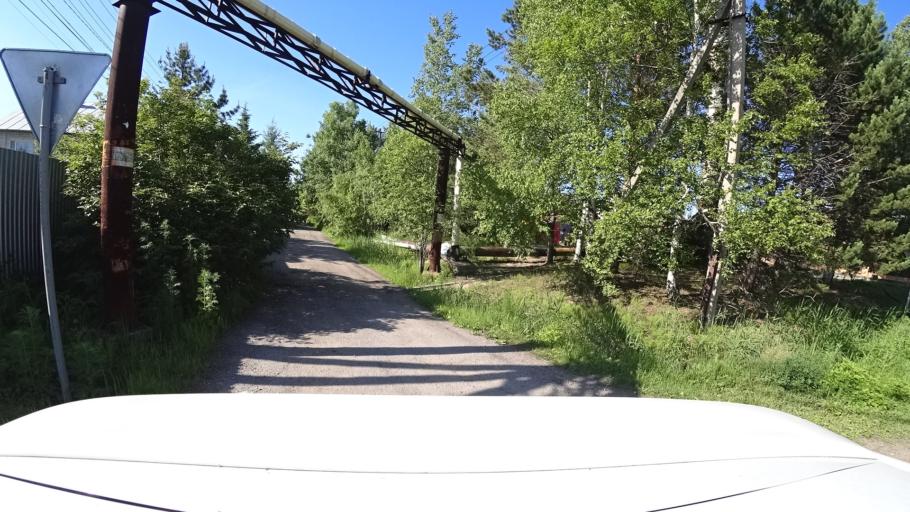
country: RU
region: Khabarovsk Krai
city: Topolevo
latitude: 48.5412
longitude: 135.1758
